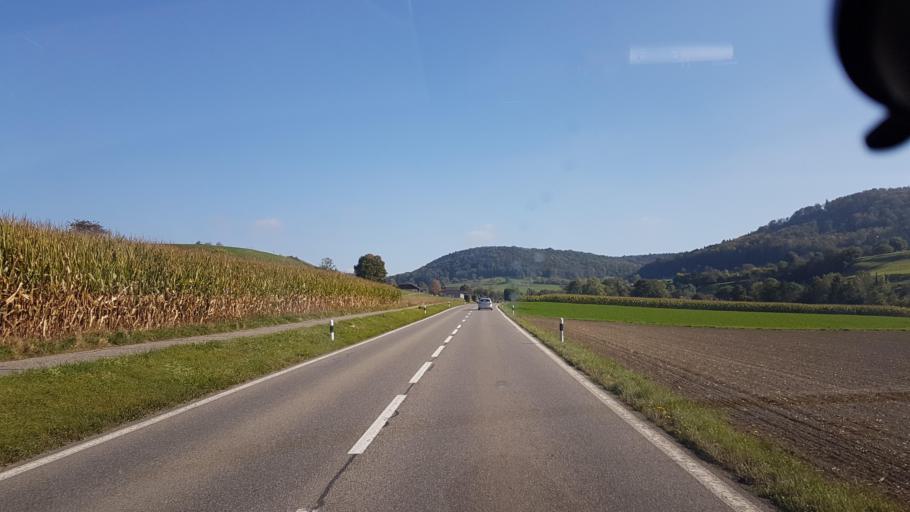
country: CH
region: Aargau
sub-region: Bezirk Laufenburg
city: Sulz
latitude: 47.4925
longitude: 8.0932
